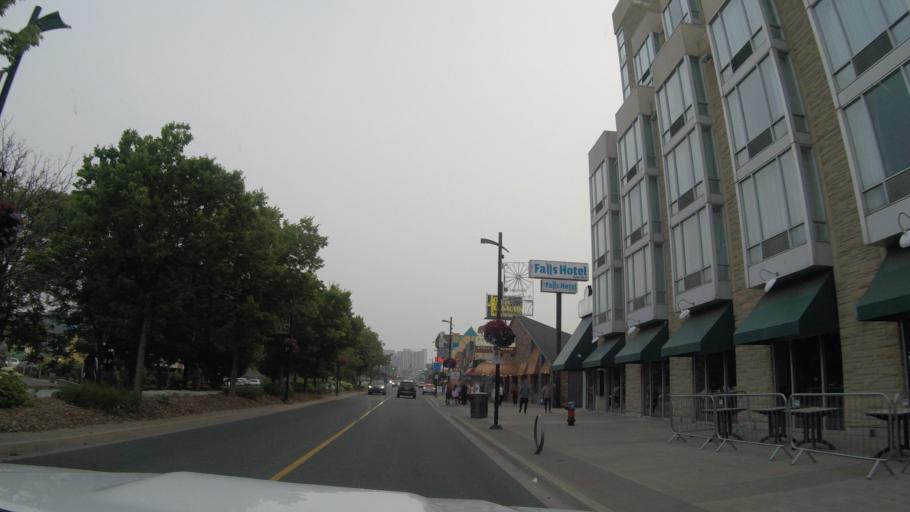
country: CA
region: Ontario
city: Niagara Falls
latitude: 43.0930
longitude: -79.0744
